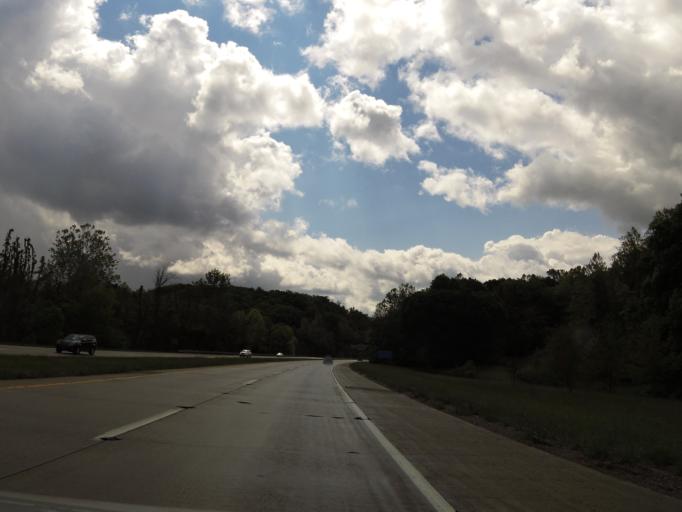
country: US
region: Ohio
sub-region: Athens County
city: Athens
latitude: 39.3507
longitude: -82.0869
